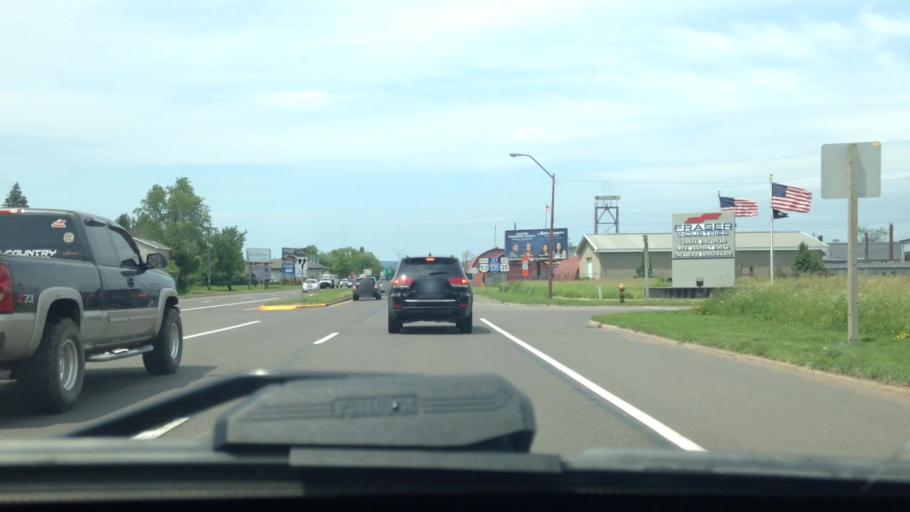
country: US
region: Wisconsin
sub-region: Douglas County
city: Superior
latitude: 46.7343
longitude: -92.0897
